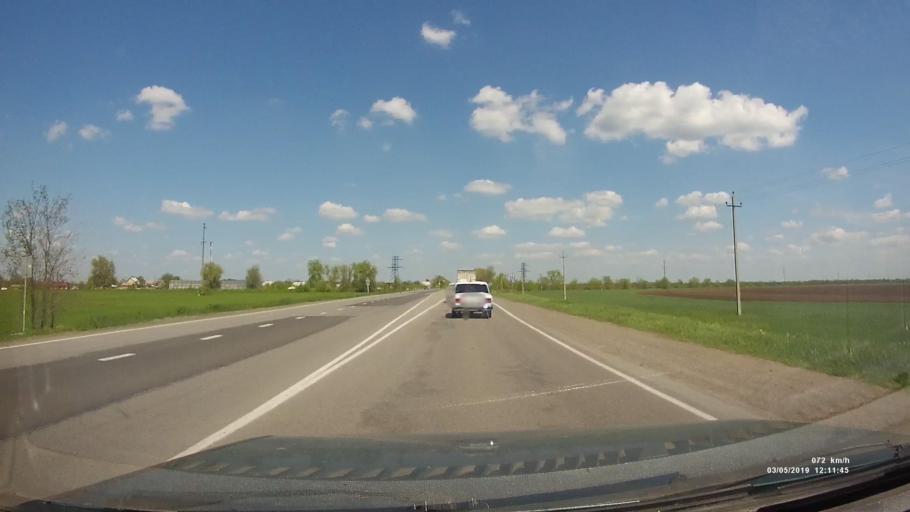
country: RU
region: Rostov
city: Bagayevskaya
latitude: 47.3140
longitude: 40.5410
